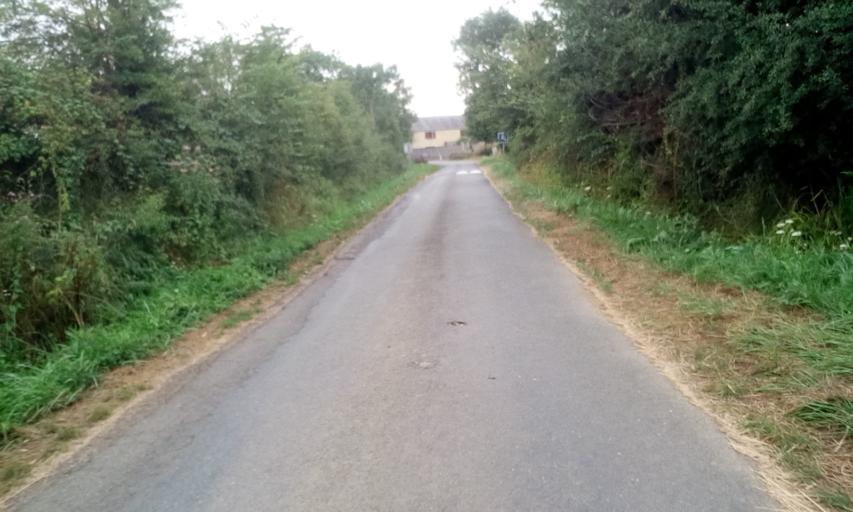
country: FR
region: Lower Normandy
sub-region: Departement du Calvados
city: Sannerville
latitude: 49.1916
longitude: -0.2198
